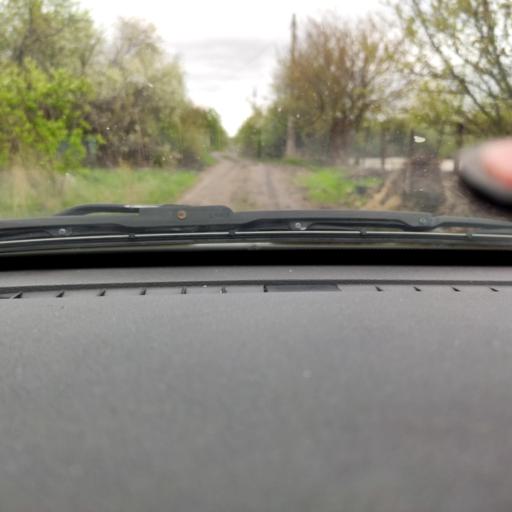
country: RU
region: Voronezj
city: Maslovka
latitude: 51.4927
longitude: 39.2143
